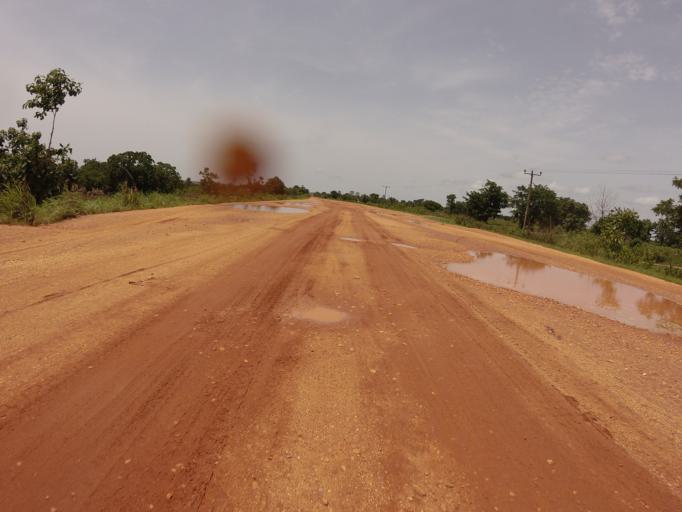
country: GH
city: Kpandae
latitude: 8.7114
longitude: 0.1490
